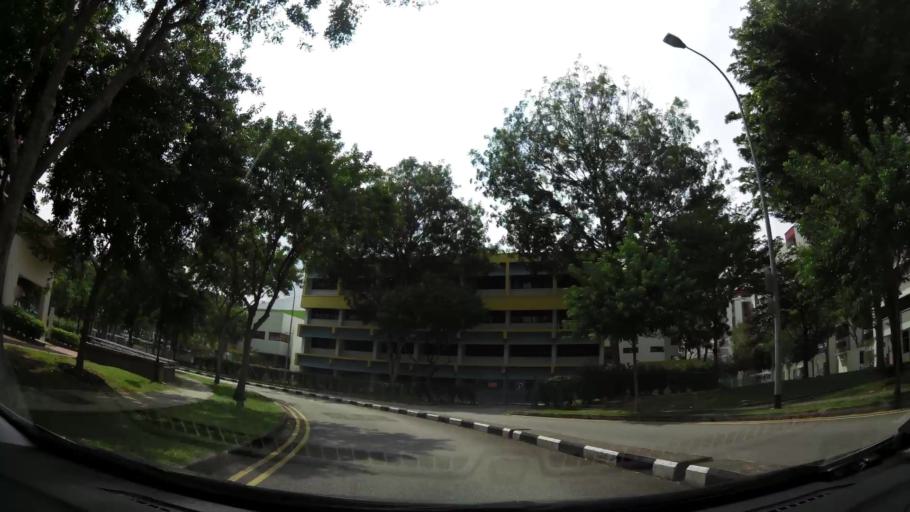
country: SG
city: Singapore
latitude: 1.3585
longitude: 103.9505
